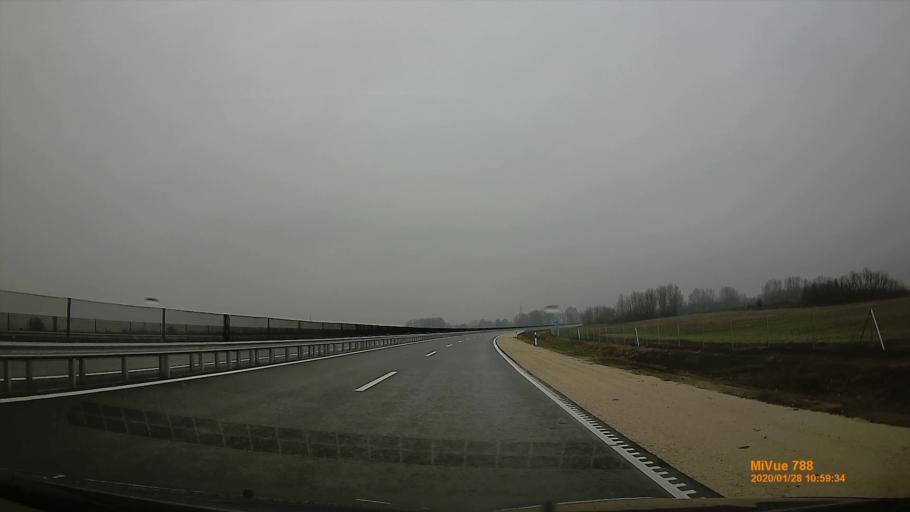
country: HU
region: Pest
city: Ullo
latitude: 47.3825
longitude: 19.3818
